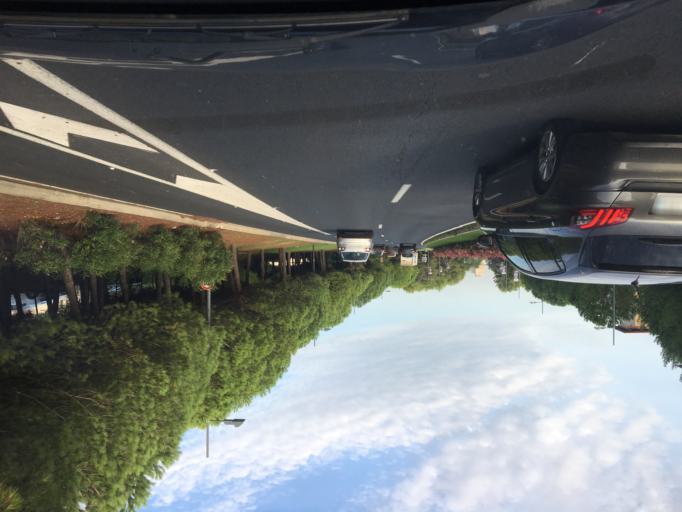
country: FR
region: Languedoc-Roussillon
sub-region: Departement de l'Herault
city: Castelnau-le-Lez
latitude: 43.6102
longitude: 3.9059
